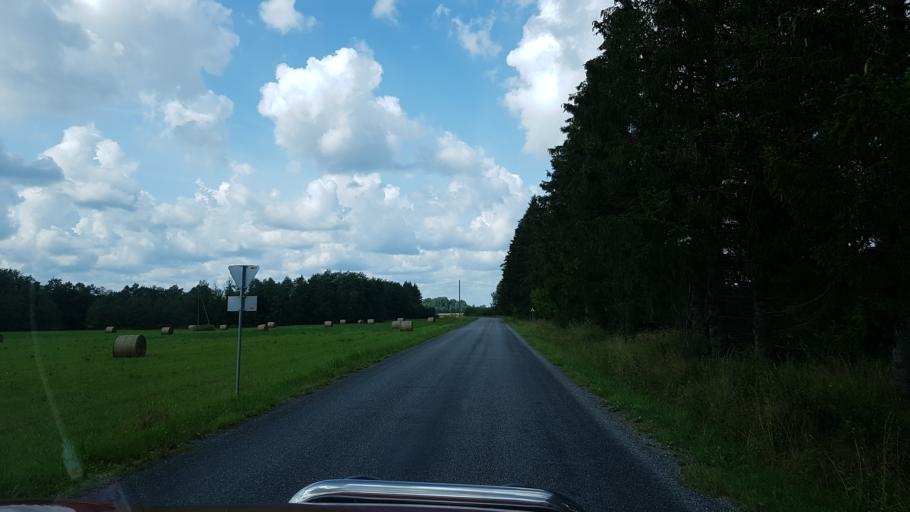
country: EE
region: Raplamaa
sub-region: Rapla vald
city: Rapla
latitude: 58.9348
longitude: 24.6444
